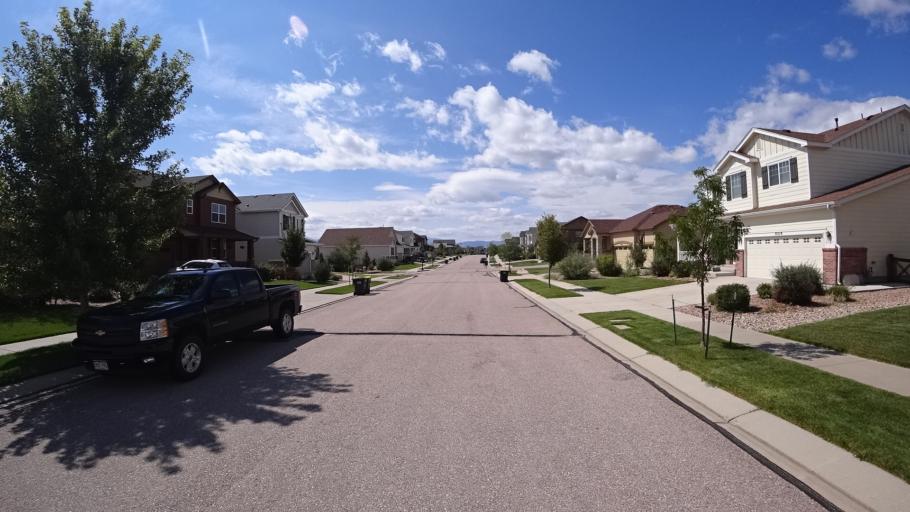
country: US
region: Colorado
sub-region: El Paso County
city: Cimarron Hills
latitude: 38.9300
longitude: -104.6759
